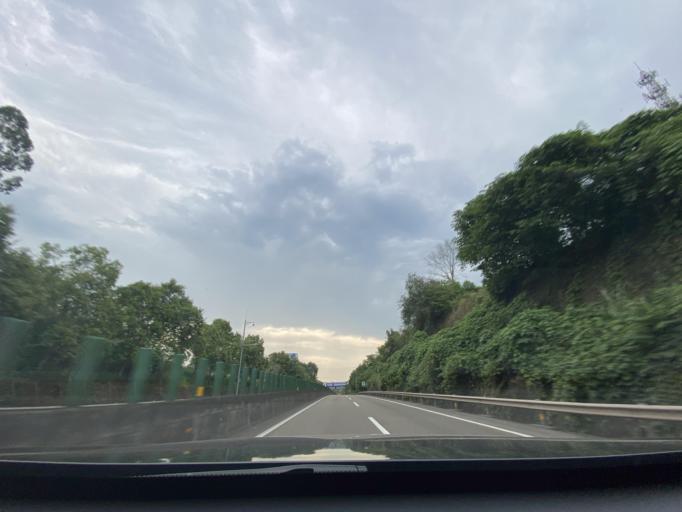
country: CN
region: Sichuan
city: Chonglong
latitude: 29.7280
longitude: 104.9200
